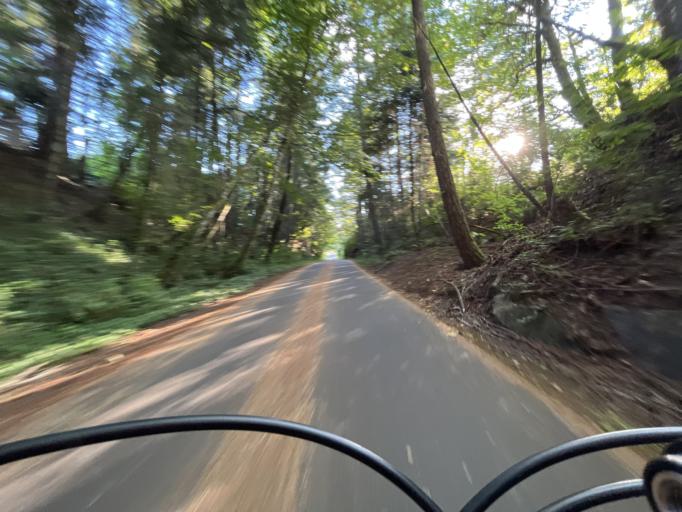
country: CA
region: British Columbia
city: Colwood
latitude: 48.4589
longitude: -123.4612
